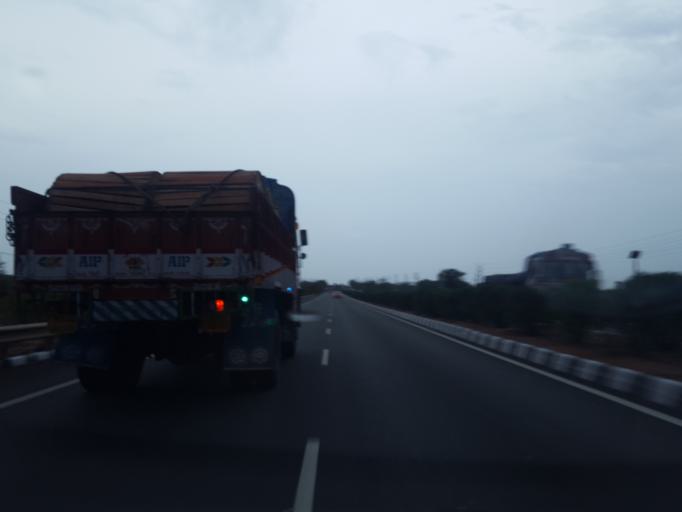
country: IN
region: Telangana
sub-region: Mahbubnagar
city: Farrukhnagar
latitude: 17.1248
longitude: 78.2759
